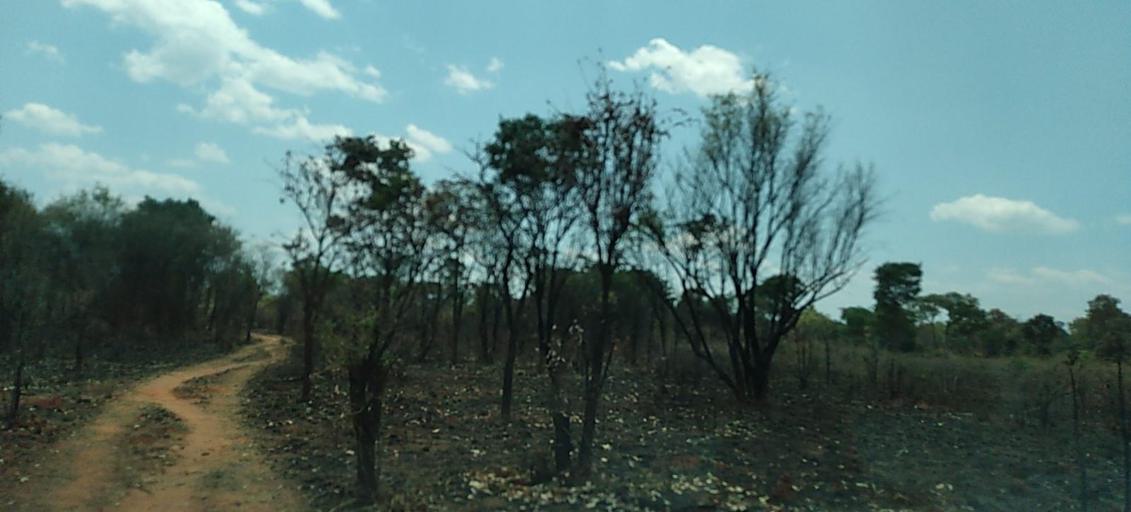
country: ZM
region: Central
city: Kapiri Mposhi
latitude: -13.6303
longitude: 28.7715
